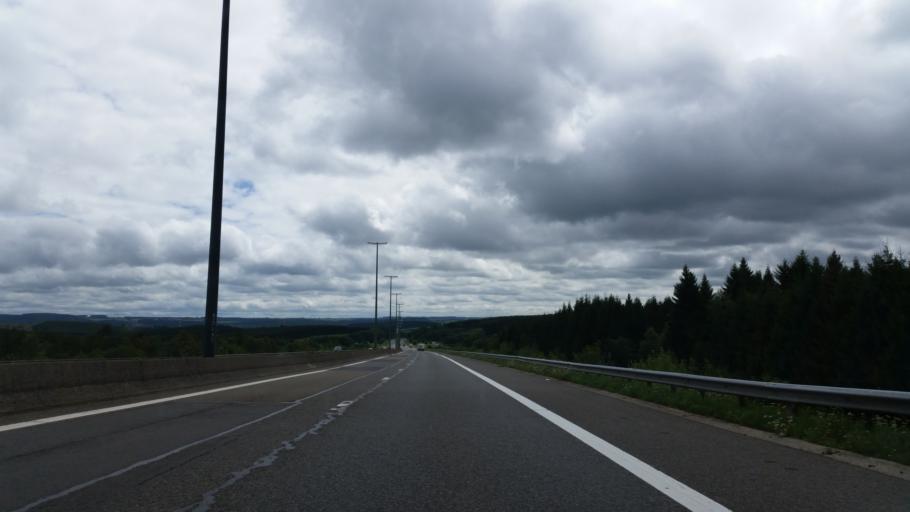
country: BE
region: Wallonia
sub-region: Province du Luxembourg
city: Houffalize
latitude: 50.1824
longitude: 5.7830
